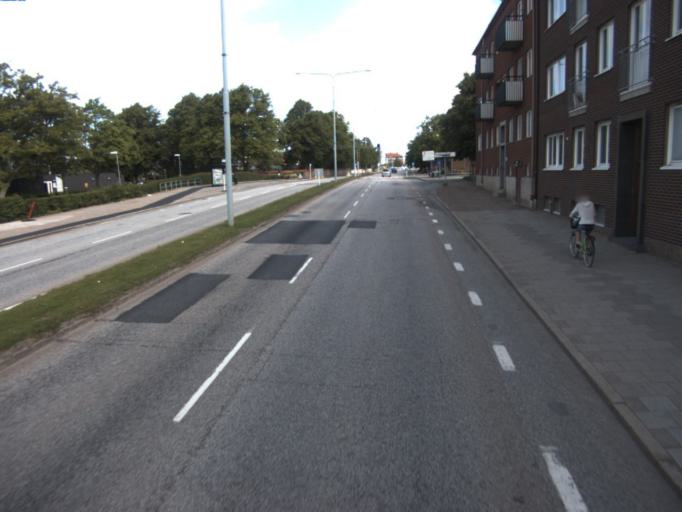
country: SE
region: Skane
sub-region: Helsingborg
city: Helsingborg
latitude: 56.0455
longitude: 12.7081
